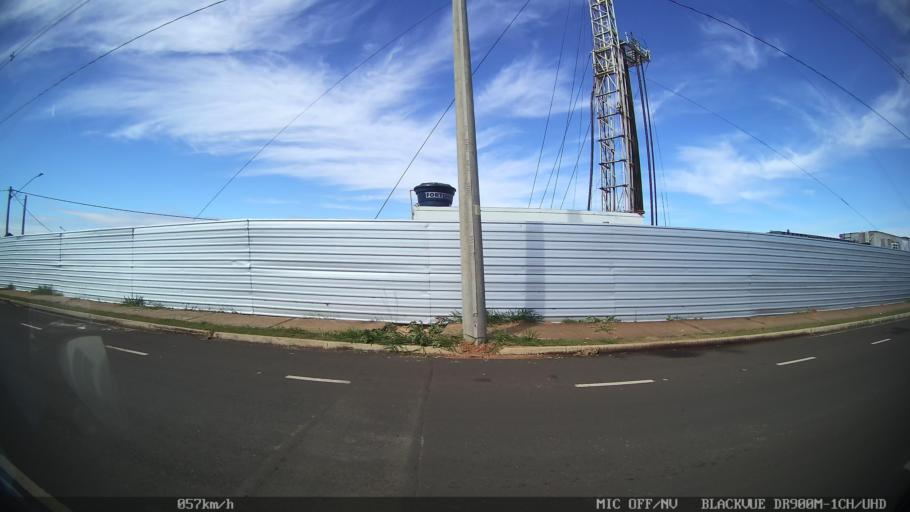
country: BR
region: Sao Paulo
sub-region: Sao Jose Do Rio Preto
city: Sao Jose do Rio Preto
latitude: -20.8574
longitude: -49.3792
